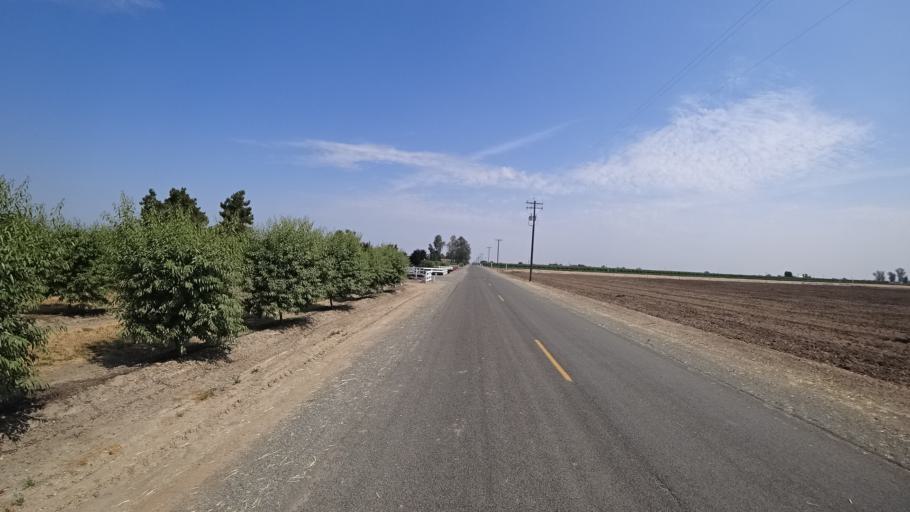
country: US
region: California
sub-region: Fresno County
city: Riverdale
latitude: 36.3968
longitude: -119.7983
